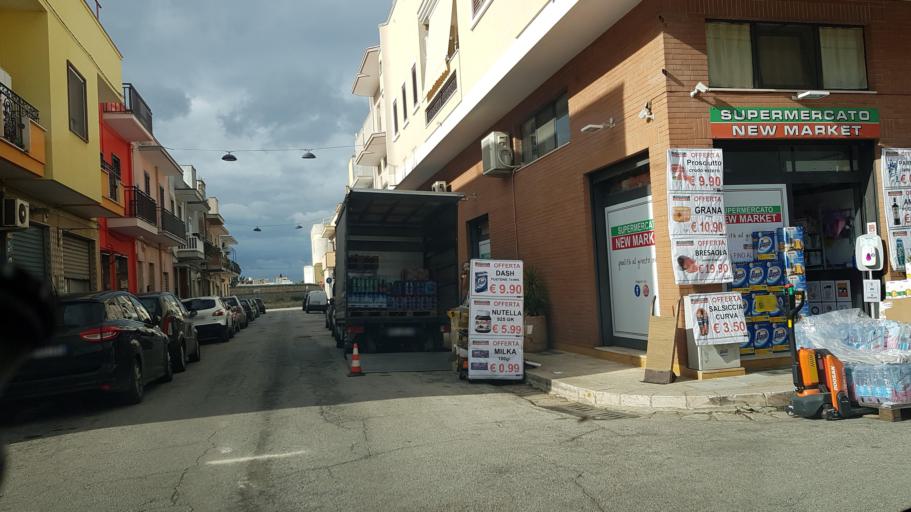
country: IT
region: Apulia
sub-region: Provincia di Brindisi
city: Francavilla Fontana
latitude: 40.5241
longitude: 17.5794
